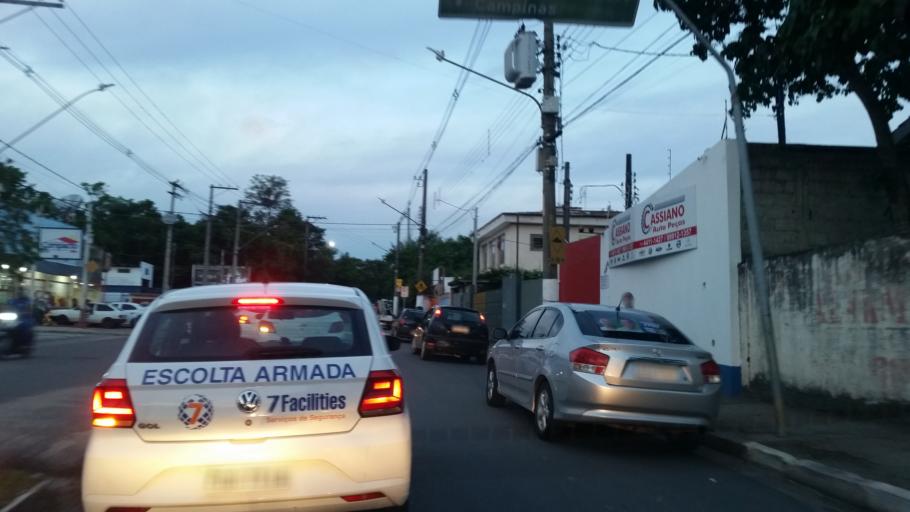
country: BR
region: Sao Paulo
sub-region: Atibaia
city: Atibaia
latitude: -23.1069
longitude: -46.5570
